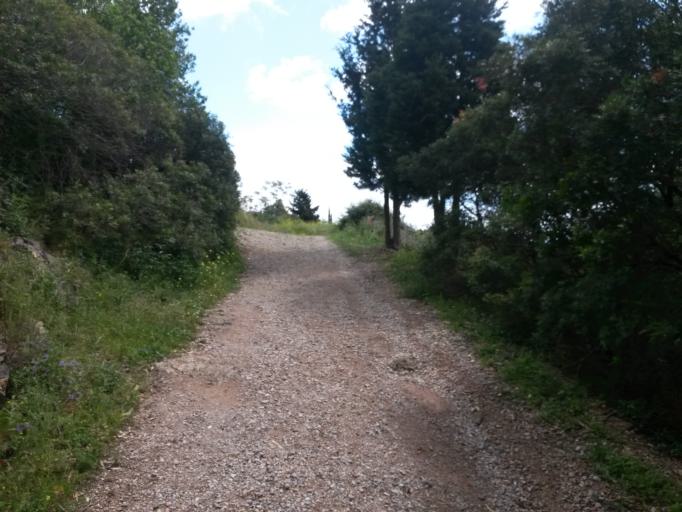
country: IT
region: Tuscany
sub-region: Provincia di Livorno
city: Rio nell'Elba
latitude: 42.8263
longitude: 10.4082
